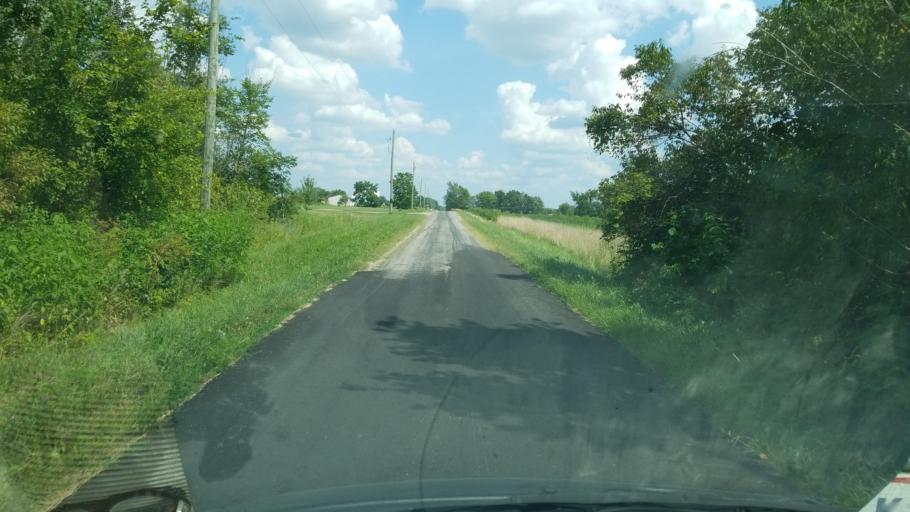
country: US
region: Ohio
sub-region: Union County
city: Richwood
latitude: 40.3998
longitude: -83.4621
